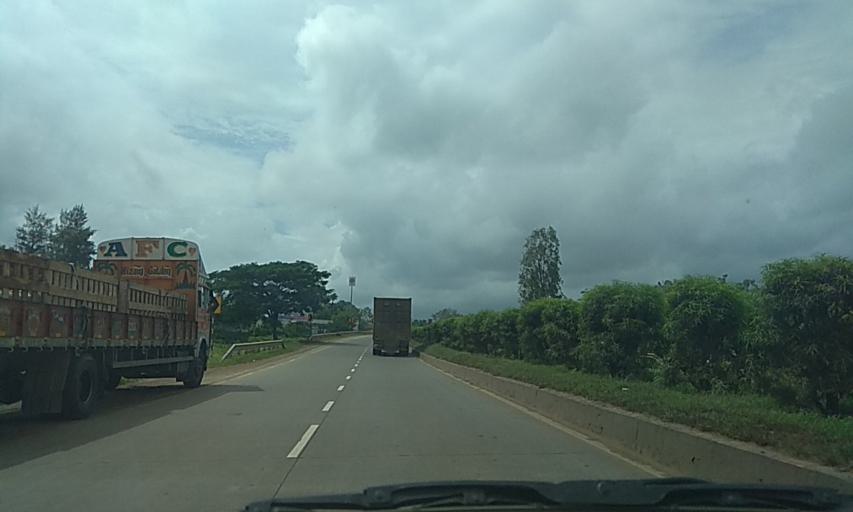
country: IN
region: Maharashtra
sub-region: Kolhapur
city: Kolhapur
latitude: 16.6532
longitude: 74.2697
